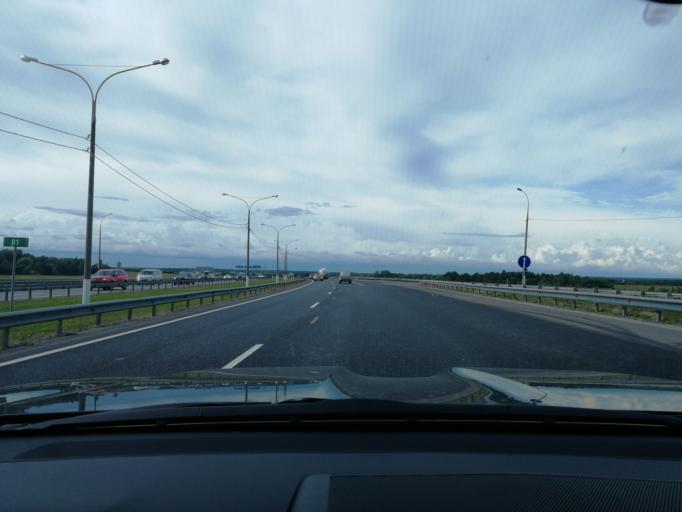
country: RU
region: Moskovskaya
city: Mikhnevo
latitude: 55.0782
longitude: 37.9368
